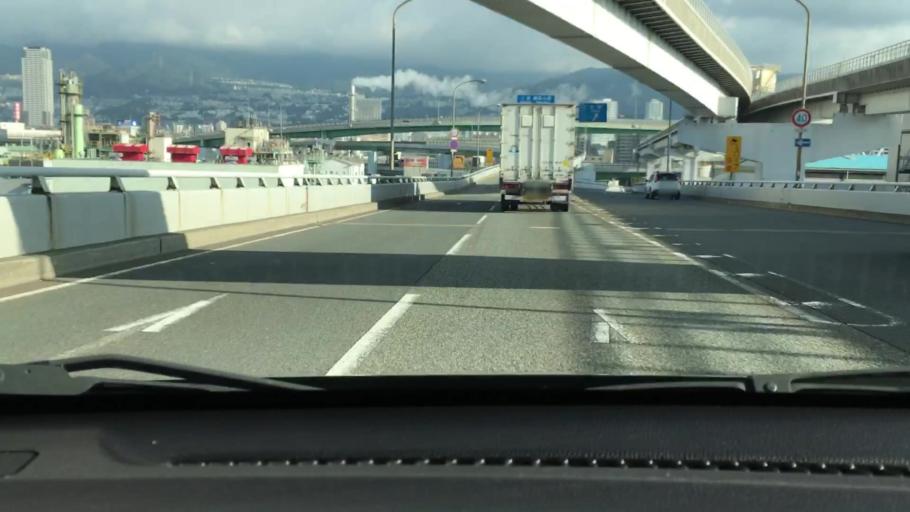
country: JP
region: Hyogo
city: Ashiya
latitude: 34.7026
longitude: 135.2672
